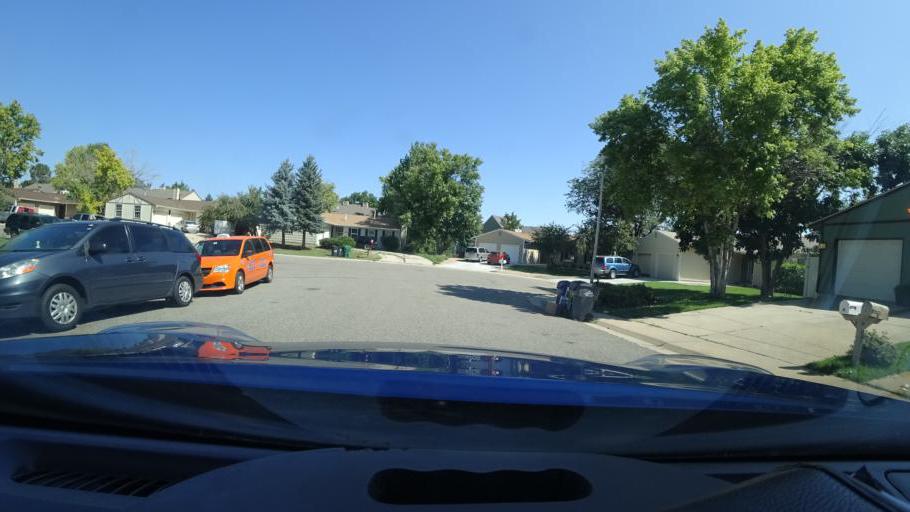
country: US
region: Colorado
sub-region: Adams County
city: Aurora
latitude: 39.6852
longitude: -104.8199
